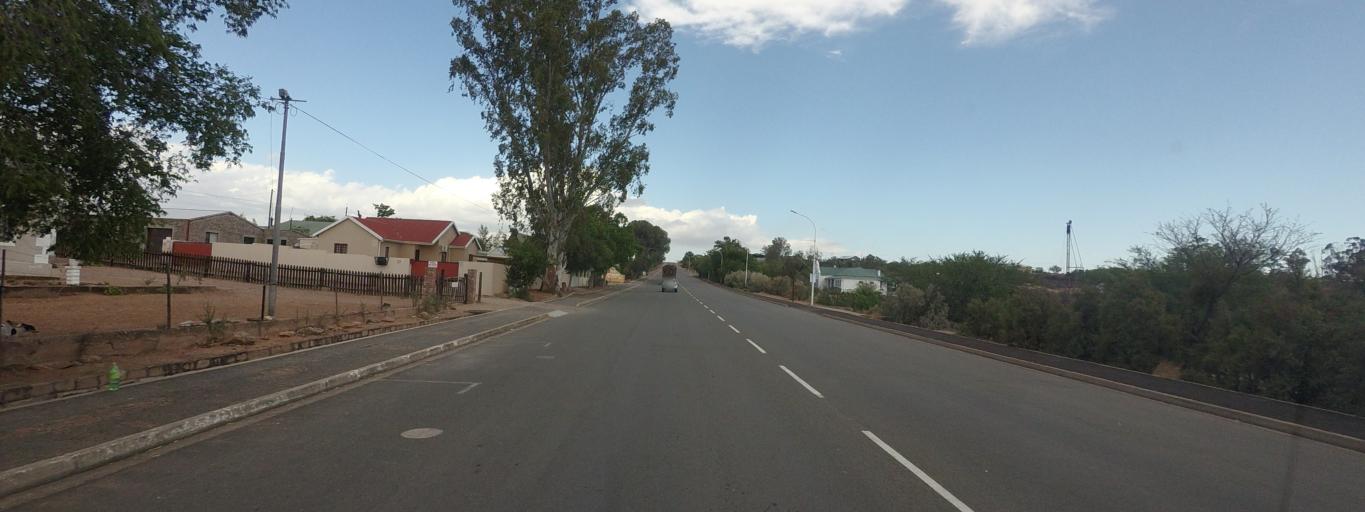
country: ZA
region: Western Cape
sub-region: Eden District Municipality
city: Ladismith
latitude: -33.5312
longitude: 21.6946
